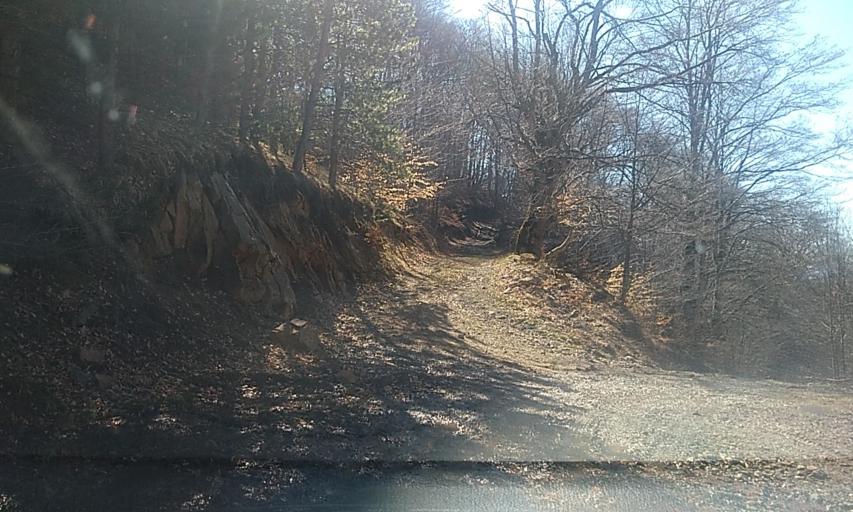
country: RS
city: Radovnica
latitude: 42.3534
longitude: 22.3365
